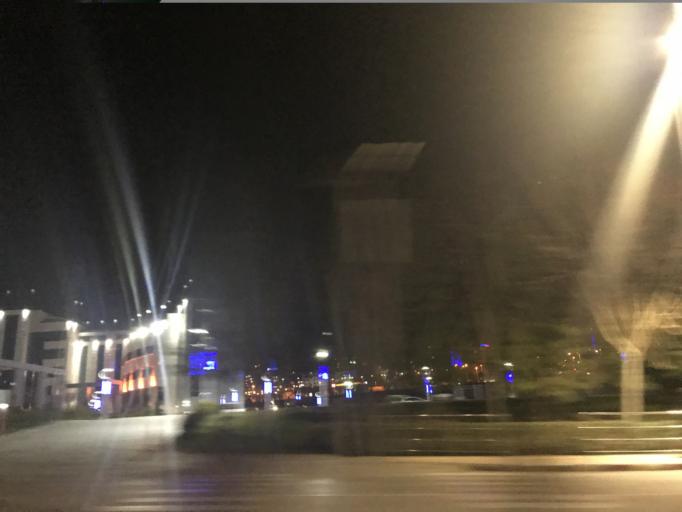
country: TR
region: Karabuk
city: Karabuk
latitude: 41.2152
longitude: 32.6527
